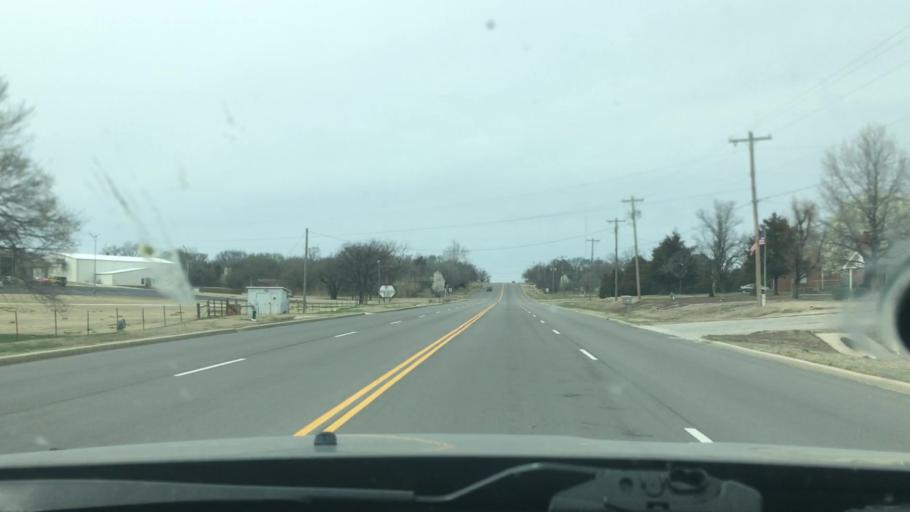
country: US
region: Oklahoma
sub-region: Seminole County
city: Seminole
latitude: 35.2521
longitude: -96.7053
